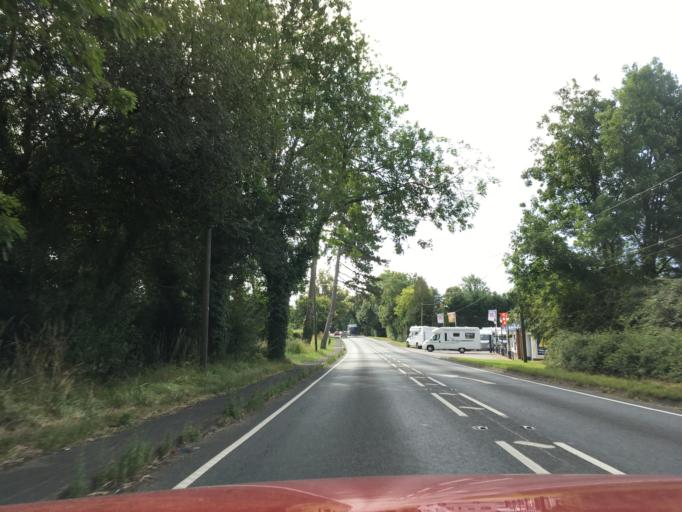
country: GB
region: England
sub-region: Hampshire
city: Bishops Waltham
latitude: 50.9709
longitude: -1.2526
